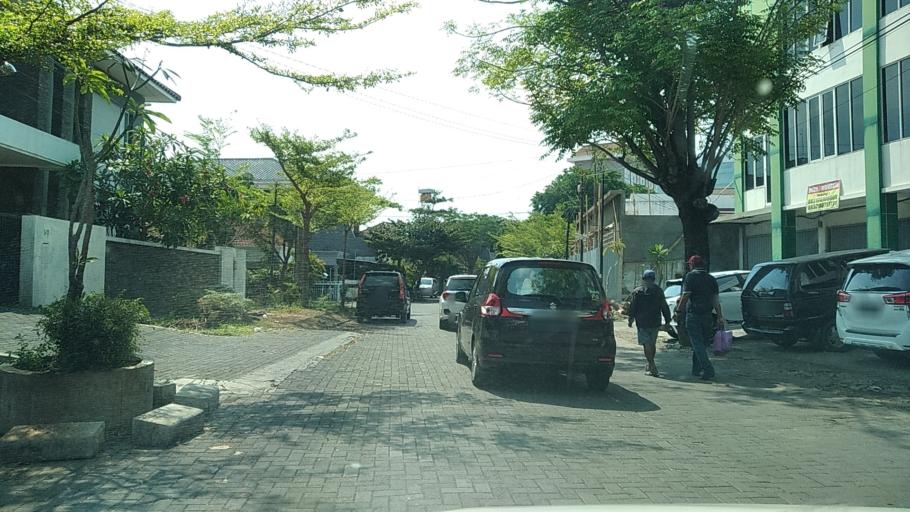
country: ID
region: Central Java
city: Semarang
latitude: -6.9893
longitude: 110.4285
